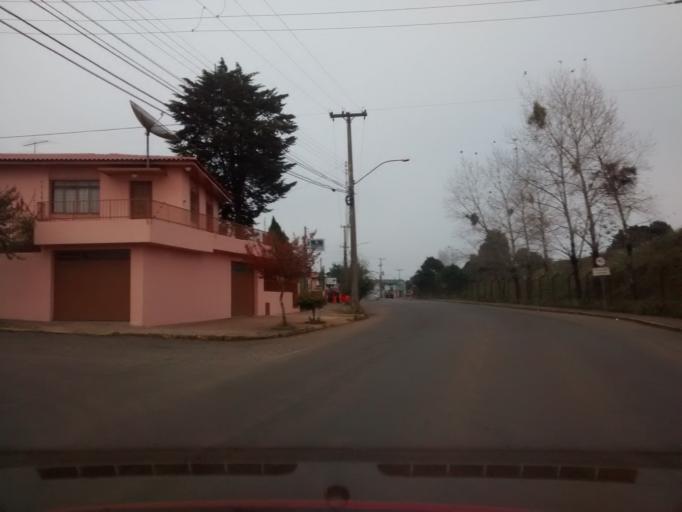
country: BR
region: Rio Grande do Sul
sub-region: Vacaria
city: Vacaria
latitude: -28.5068
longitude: -50.9450
